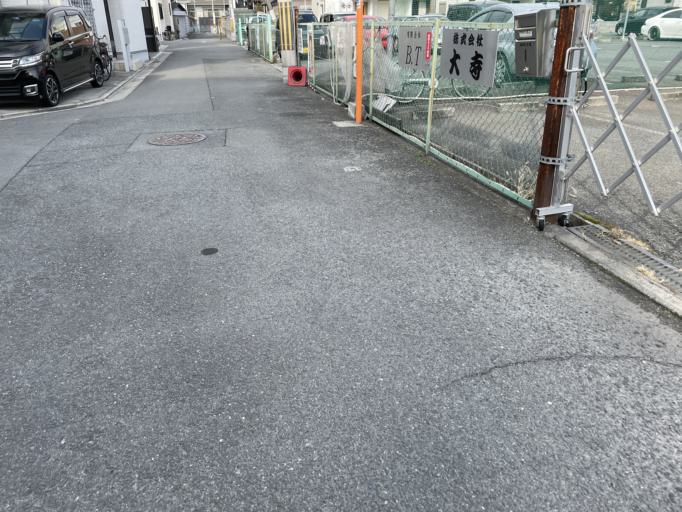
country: JP
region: Osaka
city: Daitocho
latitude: 34.6772
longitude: 135.5799
